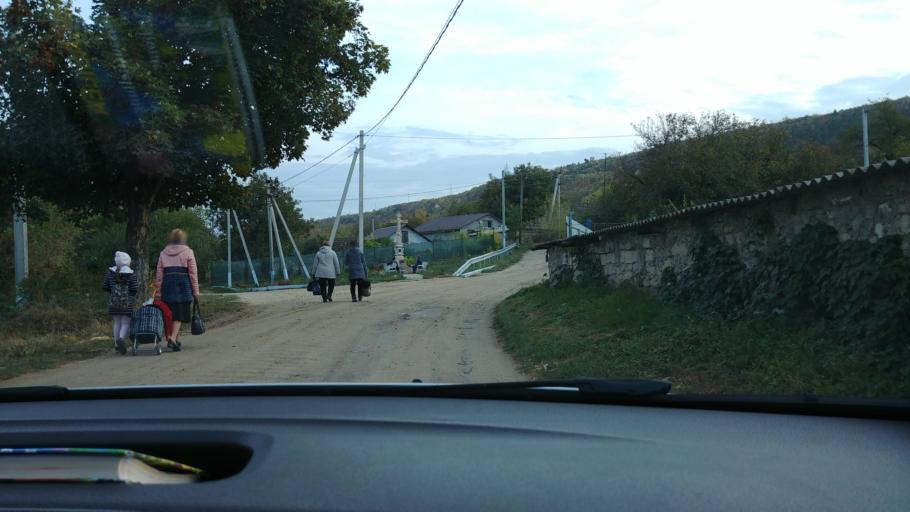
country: MD
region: Rezina
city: Saharna
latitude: 47.6905
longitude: 28.9766
